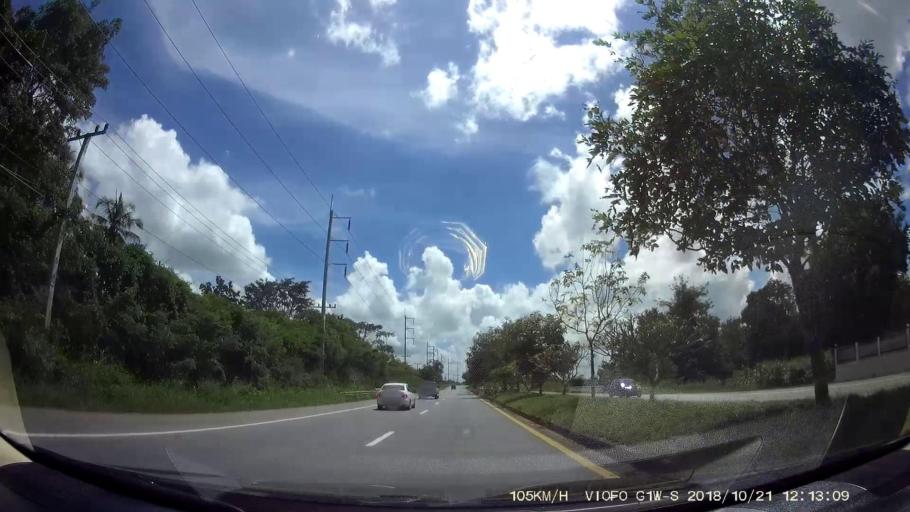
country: TH
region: Chaiyaphum
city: Chatturat
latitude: 15.3973
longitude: 101.8388
